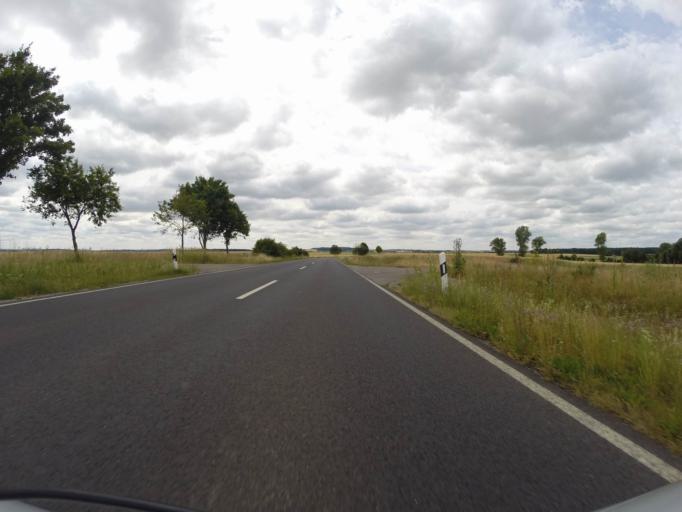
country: DE
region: Bavaria
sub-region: Regierungsbezirk Unterfranken
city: Kolitzheim
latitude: 49.9360
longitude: 10.2558
